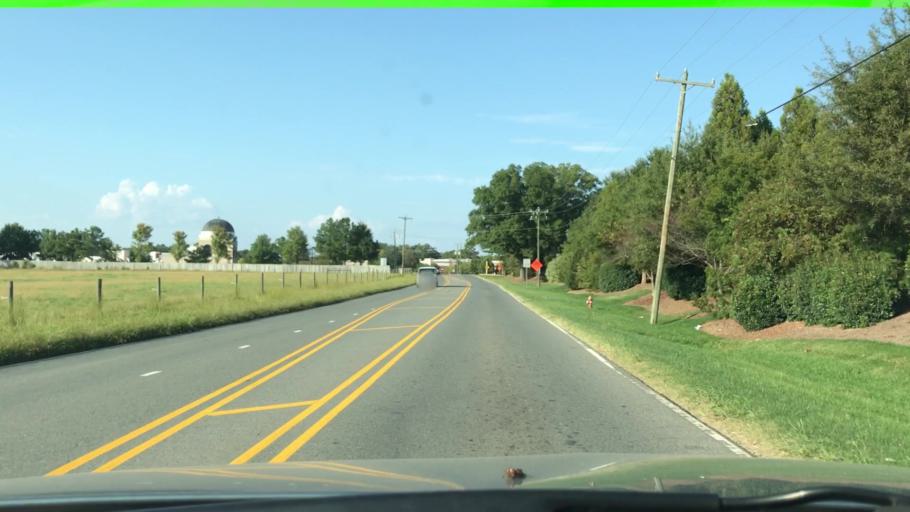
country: US
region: North Carolina
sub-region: Union County
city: Wesley Chapel
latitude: 34.9970
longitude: -80.6990
